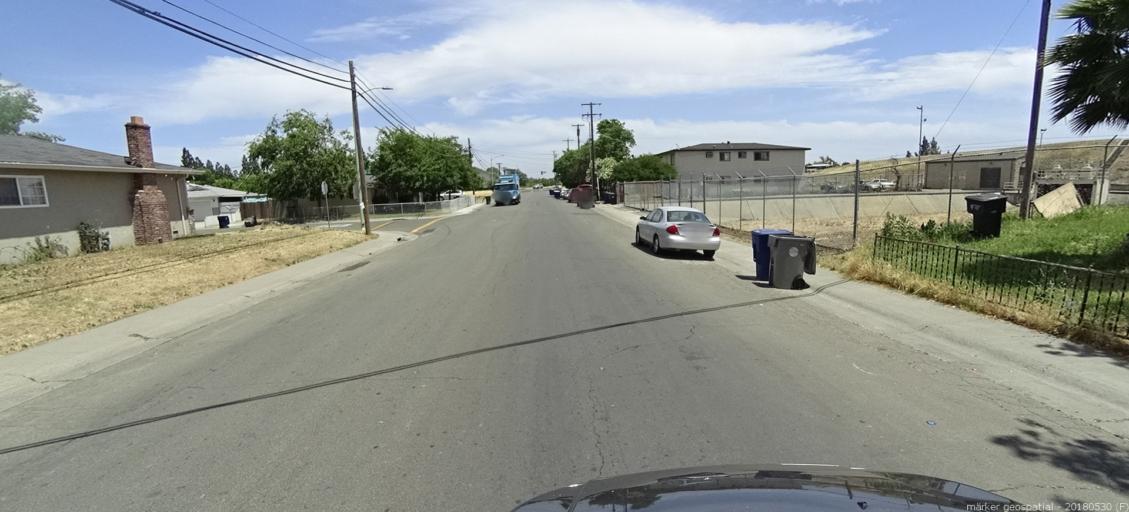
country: US
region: California
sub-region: Sacramento County
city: Sacramento
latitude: 38.6259
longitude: -121.4596
